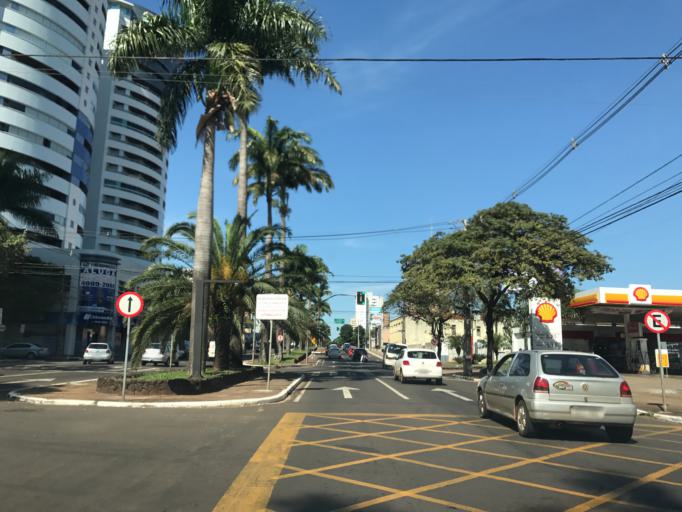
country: BR
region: Parana
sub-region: Maringa
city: Maringa
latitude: -23.4167
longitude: -51.9433
